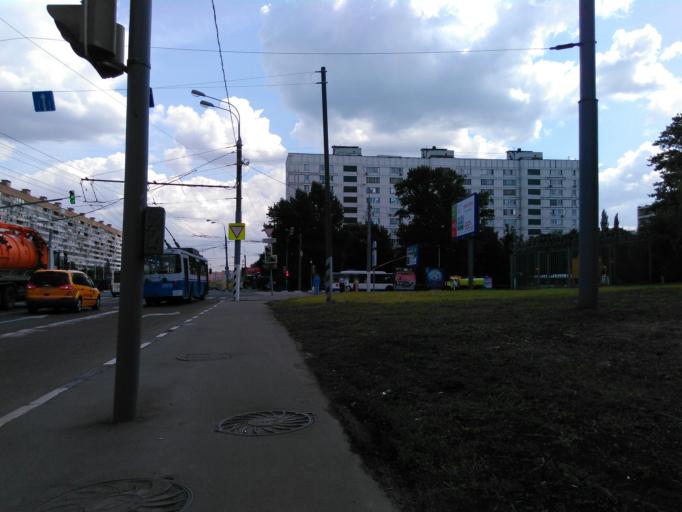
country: RU
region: Moscow
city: Zyuzino
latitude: 55.6702
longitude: 37.5844
